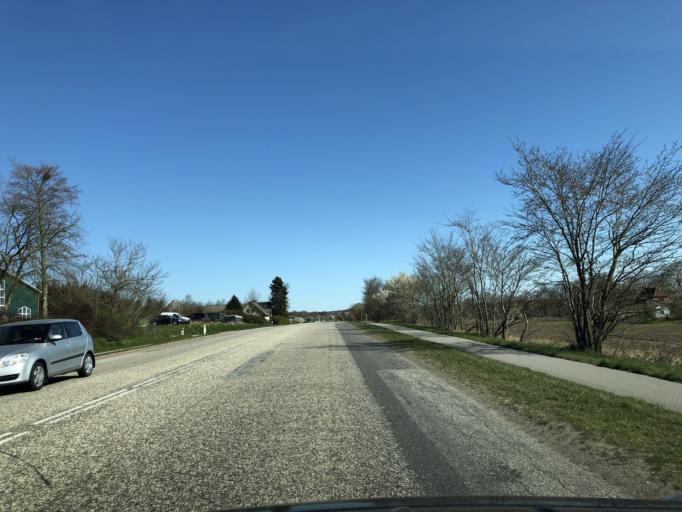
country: DK
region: North Denmark
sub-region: Rebild Kommune
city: Stovring
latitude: 56.9155
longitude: 9.8543
